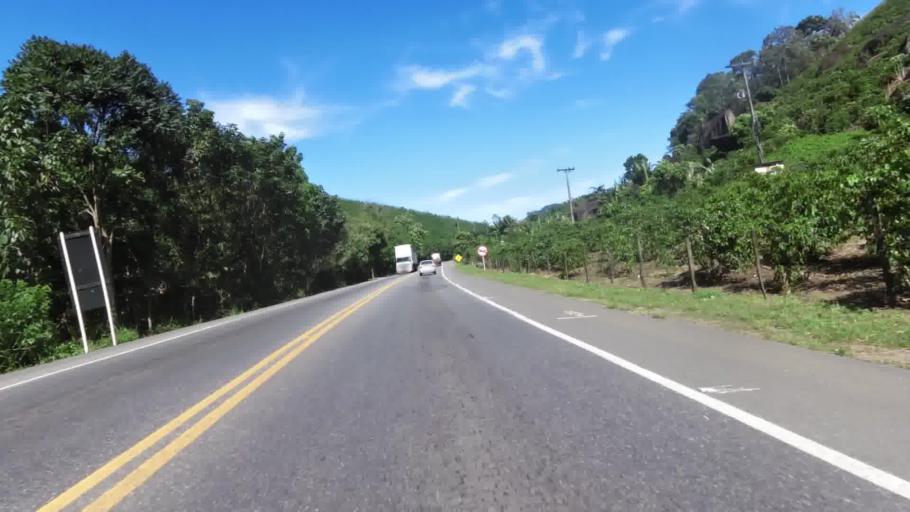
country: BR
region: Espirito Santo
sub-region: Iconha
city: Iconha
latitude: -20.8321
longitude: -40.8599
